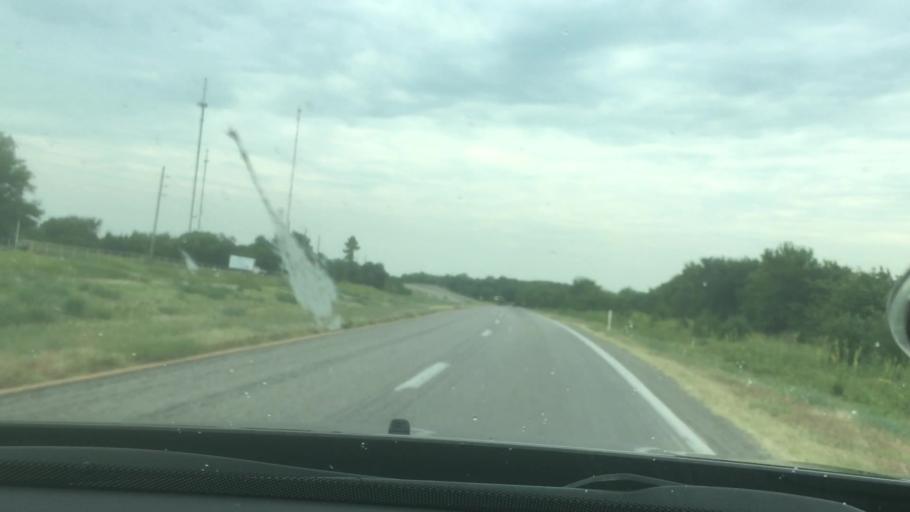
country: US
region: Oklahoma
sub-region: Pontotoc County
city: Ada
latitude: 34.7207
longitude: -96.7165
